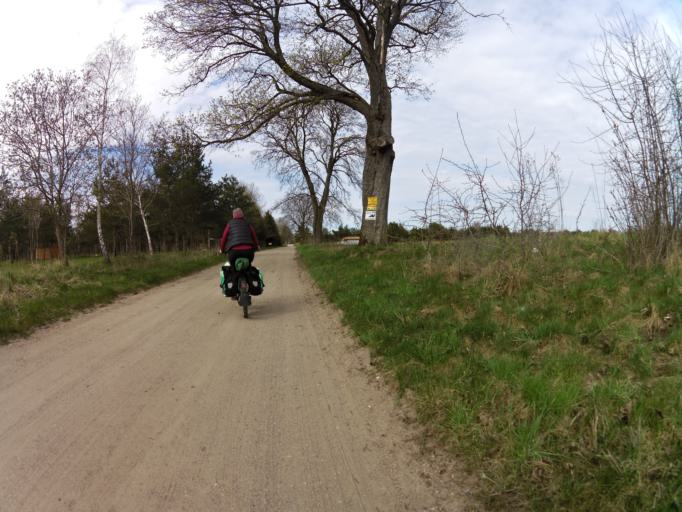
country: PL
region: West Pomeranian Voivodeship
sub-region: Powiat szczecinecki
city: Szczecinek
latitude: 53.8487
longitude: 16.6843
